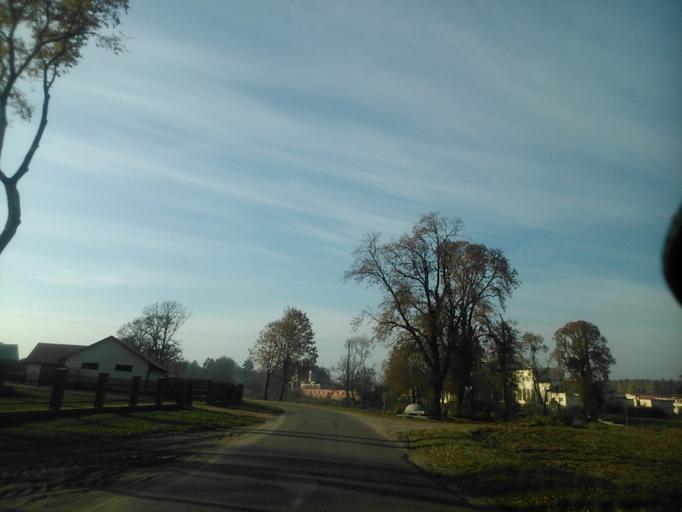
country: PL
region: Warmian-Masurian Voivodeship
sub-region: Powiat dzialdowski
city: Rybno
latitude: 53.2765
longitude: 19.9662
